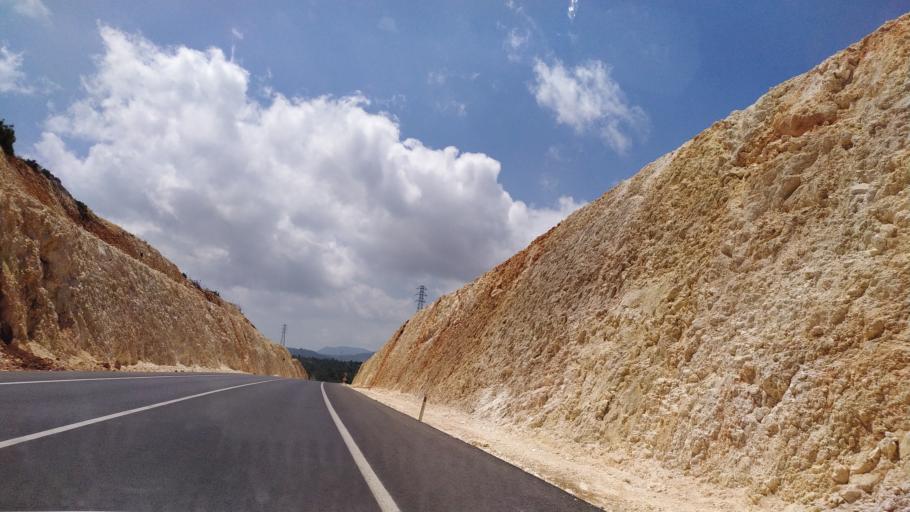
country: TR
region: Mersin
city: Gulnar
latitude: 36.2680
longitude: 33.3699
